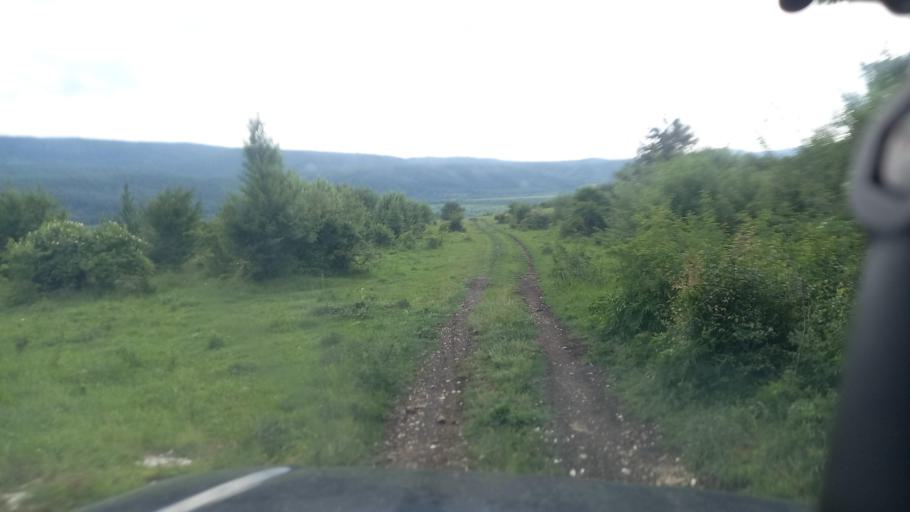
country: RU
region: Karachayevo-Cherkesiya
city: Kurdzhinovo
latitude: 44.1287
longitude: 41.0584
